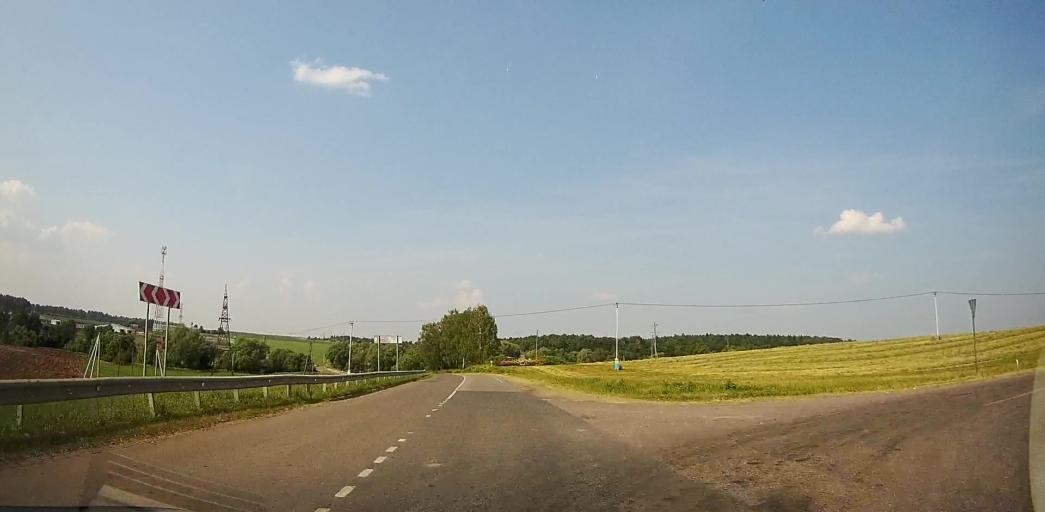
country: RU
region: Moskovskaya
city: Il'inskoye
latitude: 55.2905
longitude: 37.9425
